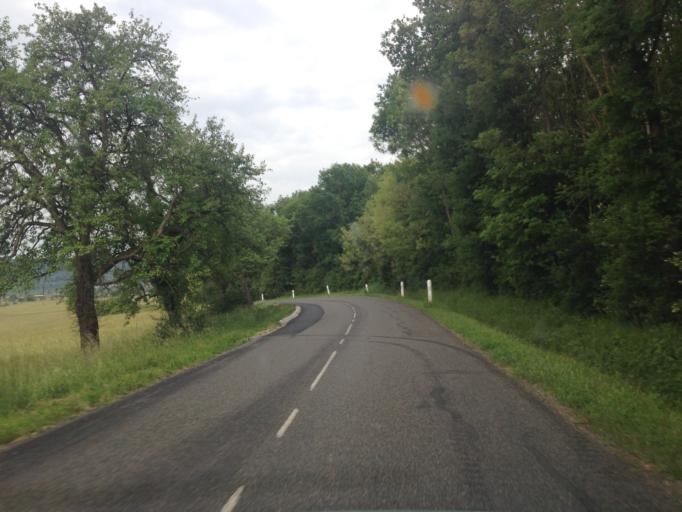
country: FR
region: Alsace
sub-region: Departement du Bas-Rhin
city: Neuwiller-les-Saverne
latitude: 48.8321
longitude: 7.4355
